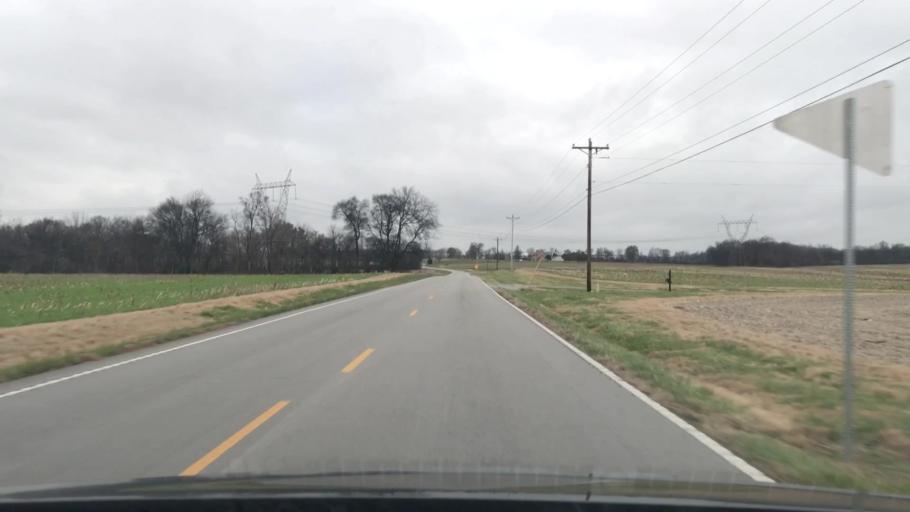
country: US
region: Kentucky
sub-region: Todd County
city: Guthrie
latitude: 36.6649
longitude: -87.1983
